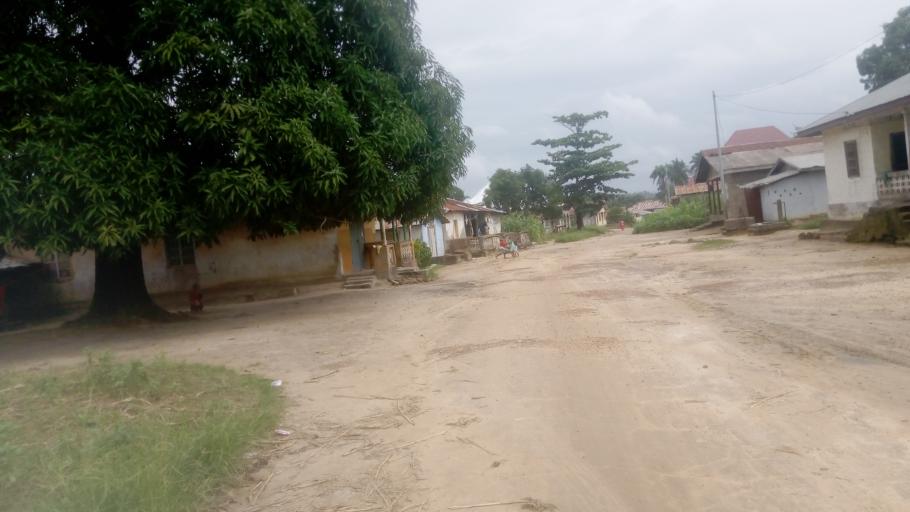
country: SL
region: Northern Province
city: Lunsar
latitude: 8.6884
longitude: -12.5388
